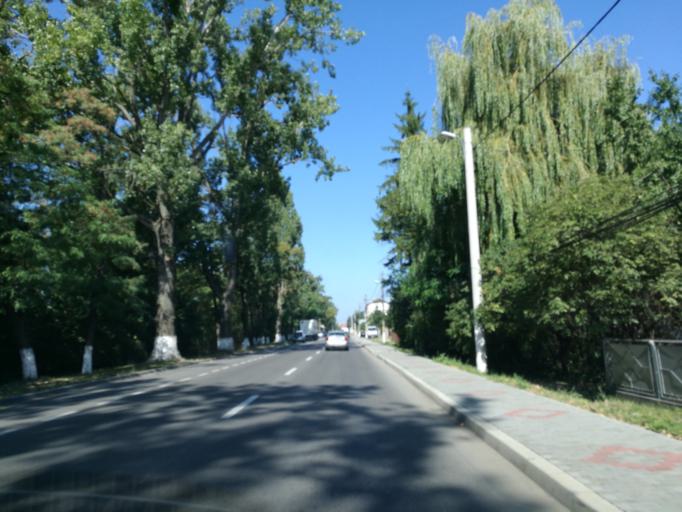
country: RO
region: Suceava
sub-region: Municipiul Suceava
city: Radauti
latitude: 47.8342
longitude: 25.9310
